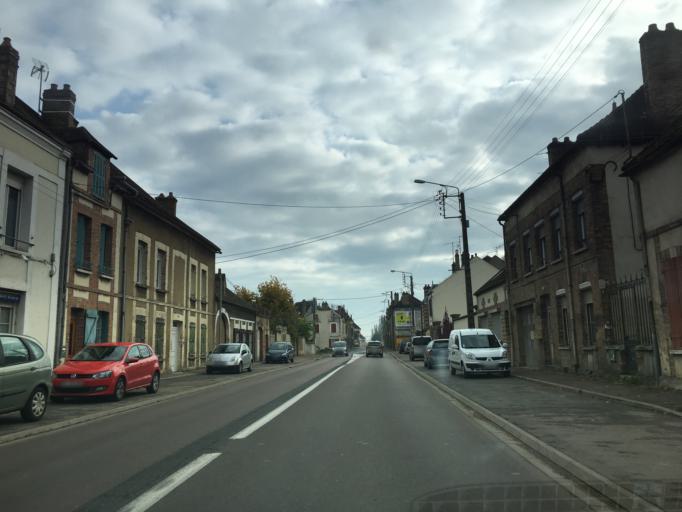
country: FR
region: Bourgogne
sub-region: Departement de l'Yonne
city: Pont-sur-Yonne
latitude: 48.2901
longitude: 3.2019
